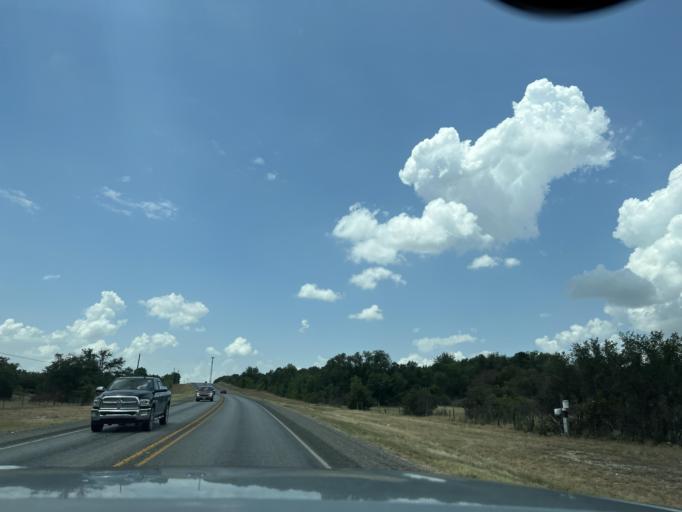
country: US
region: Texas
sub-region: Parker County
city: Springtown
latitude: 32.9213
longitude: -97.7107
